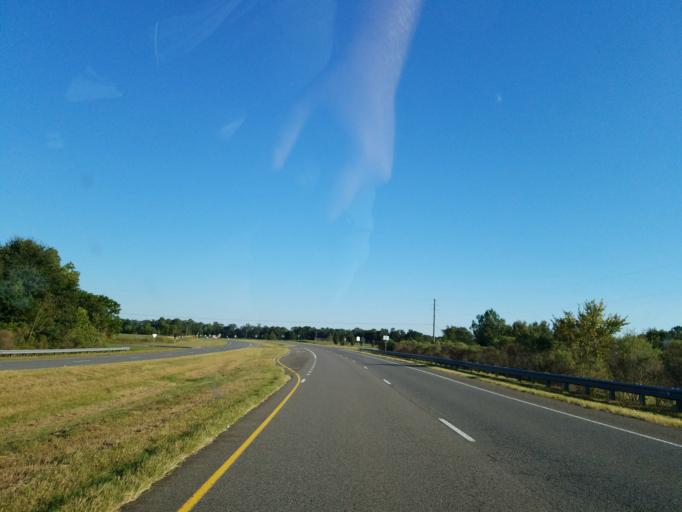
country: US
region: Georgia
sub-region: Lee County
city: Leesburg
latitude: 31.7254
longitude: -84.1813
